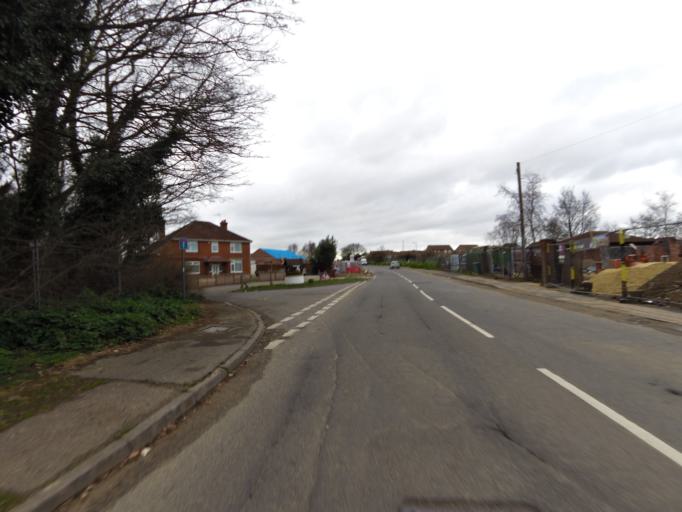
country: GB
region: England
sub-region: Norfolk
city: Hopton on Sea
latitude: 52.5400
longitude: 1.7213
